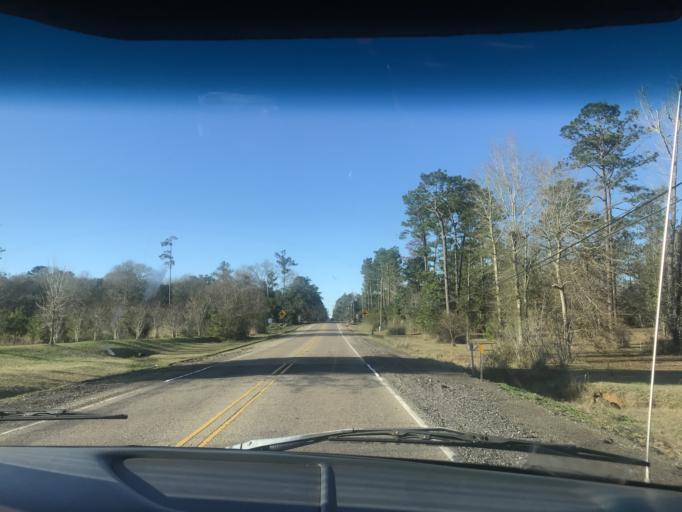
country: US
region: Louisiana
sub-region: Saint Tammany Parish
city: Covington
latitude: 30.5755
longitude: -90.1618
